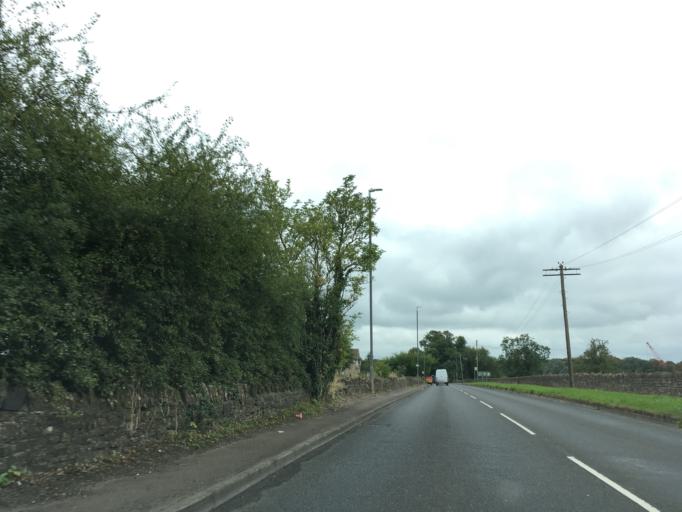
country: GB
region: England
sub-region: Bath and North East Somerset
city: Keynsham
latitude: 51.4252
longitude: -2.4855
